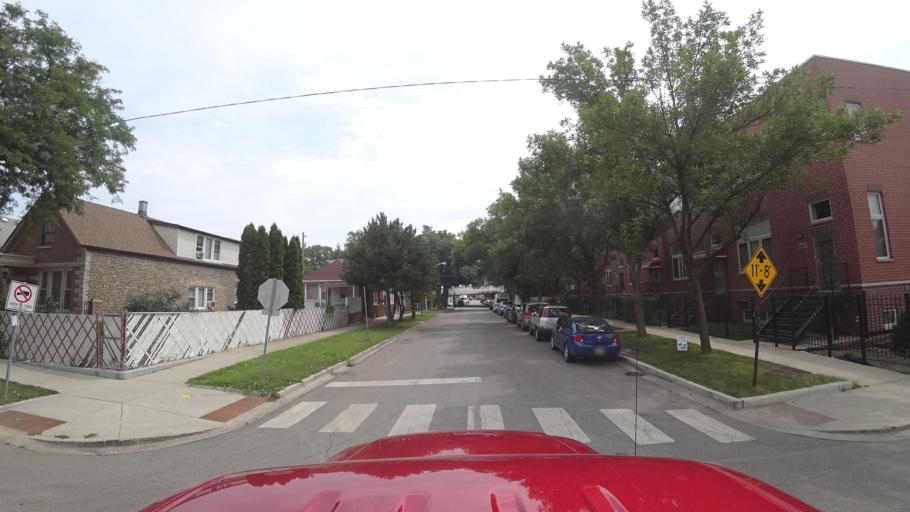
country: US
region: Illinois
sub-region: Cook County
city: Chicago
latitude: 41.8322
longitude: -87.6778
